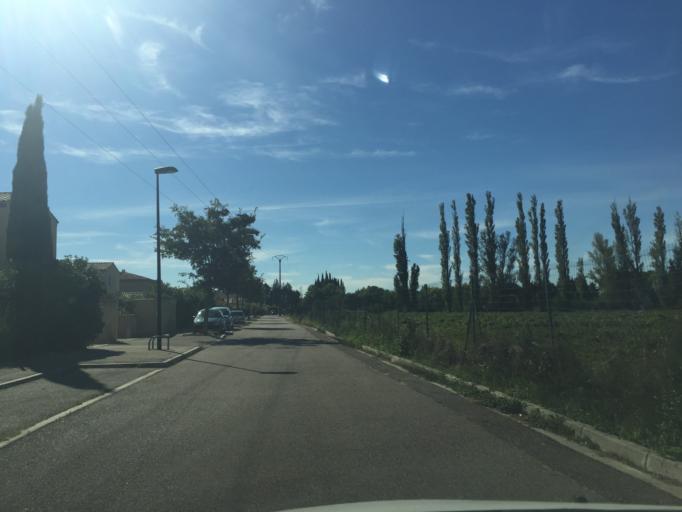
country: FR
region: Provence-Alpes-Cote d'Azur
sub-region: Departement du Vaucluse
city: Orange
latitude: 44.1447
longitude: 4.7904
